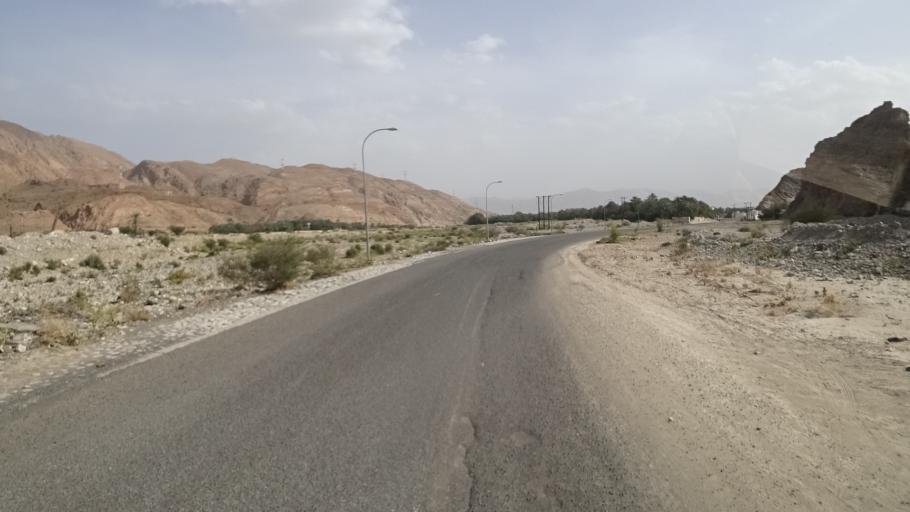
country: OM
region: Muhafazat Masqat
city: Bawshar
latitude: 23.3954
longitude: 58.5203
